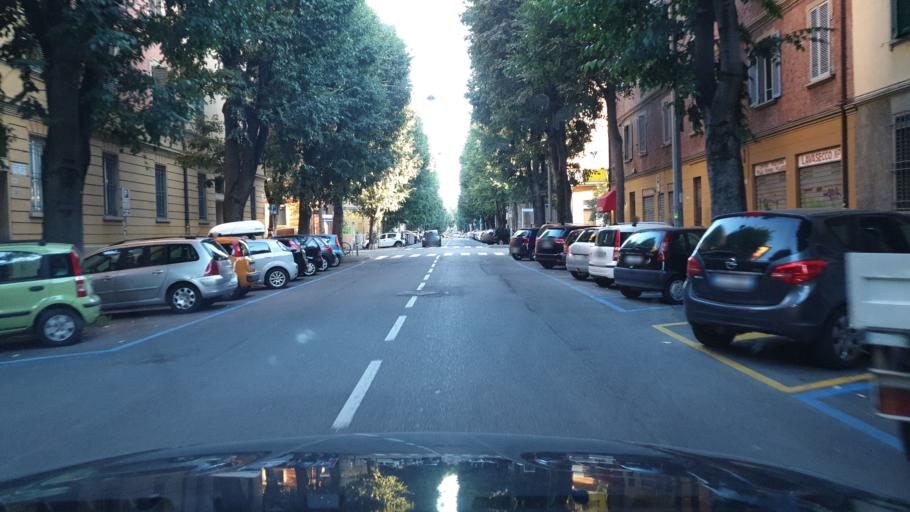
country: IT
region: Emilia-Romagna
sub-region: Provincia di Bologna
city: Bologna
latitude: 44.4966
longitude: 11.3625
